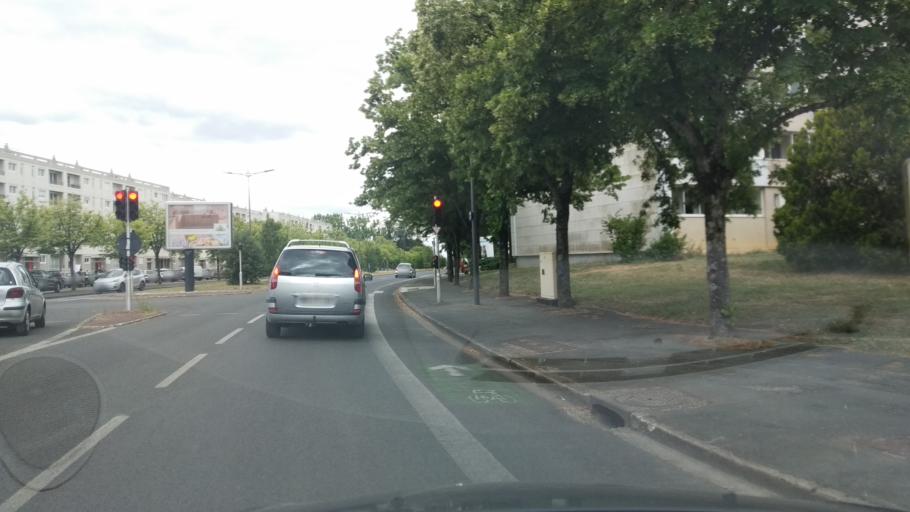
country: FR
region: Poitou-Charentes
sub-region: Departement de la Vienne
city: Poitiers
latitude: 46.5899
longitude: 0.3554
